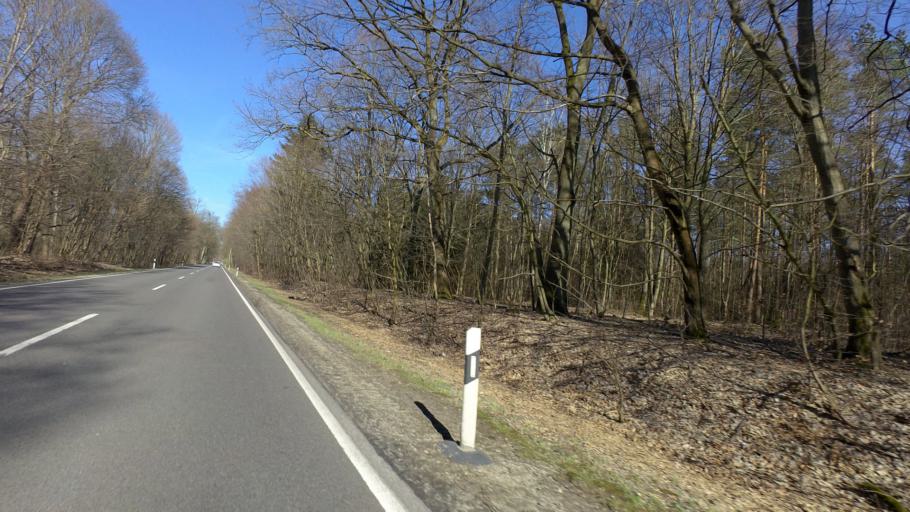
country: DE
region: Brandenburg
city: Chorin
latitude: 52.9232
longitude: 13.9112
